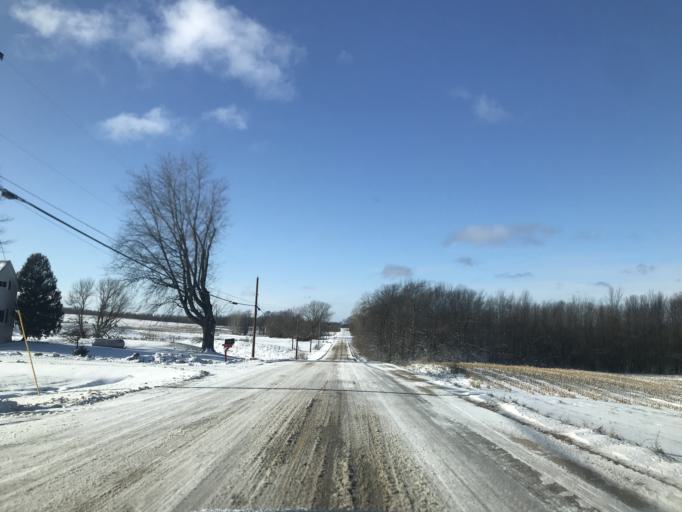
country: US
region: Wisconsin
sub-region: Door County
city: Sturgeon Bay
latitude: 44.8500
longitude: -87.4609
